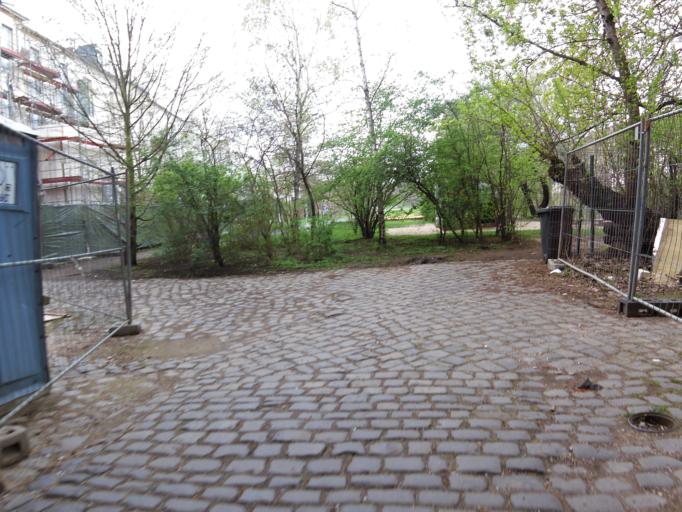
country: DE
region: Saxony
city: Leipzig
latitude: 51.3279
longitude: 12.3358
